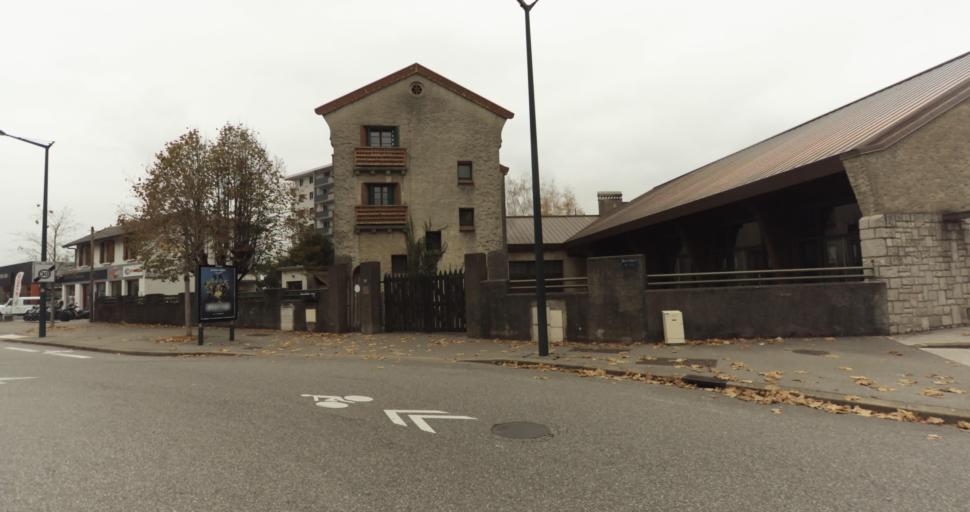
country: FR
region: Rhone-Alpes
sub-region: Departement de la Haute-Savoie
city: Metz-Tessy
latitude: 45.9232
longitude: 6.1237
